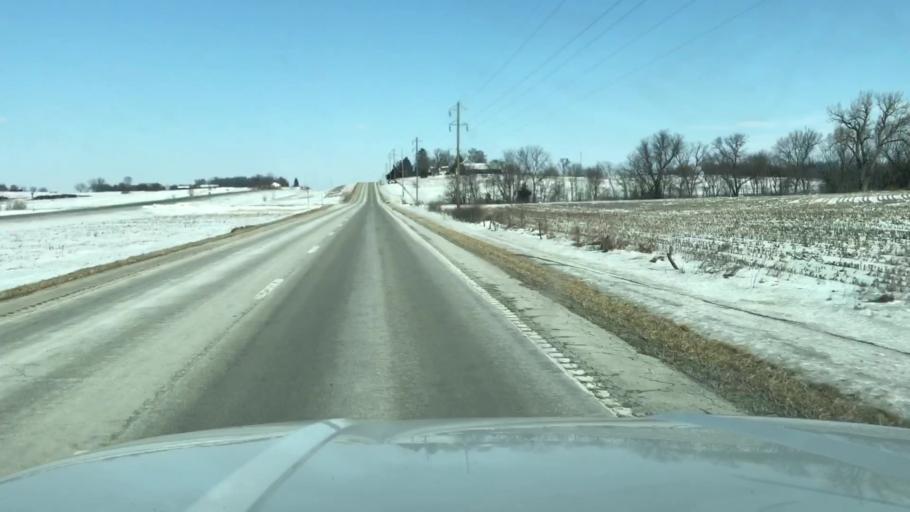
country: US
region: Missouri
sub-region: Nodaway County
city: Maryville
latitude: 40.1477
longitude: -94.8692
